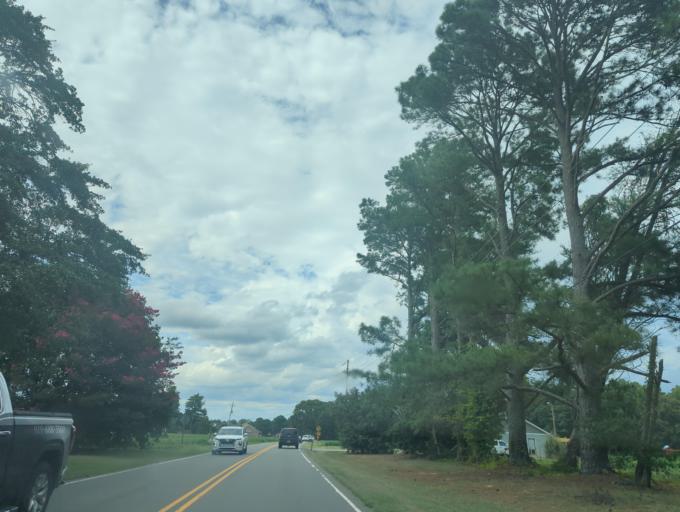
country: US
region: North Carolina
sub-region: Wake County
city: Fuquay-Varina
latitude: 35.6183
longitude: -78.7749
